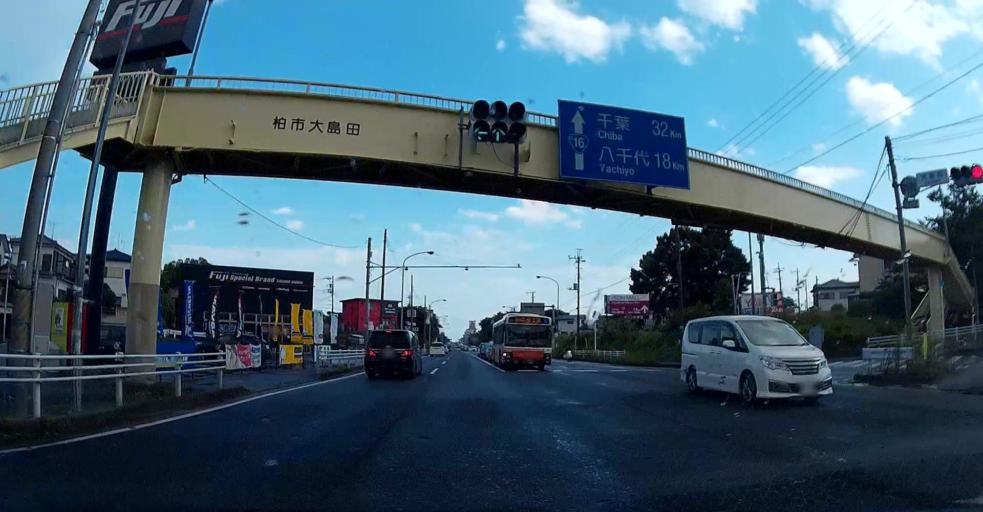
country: JP
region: Chiba
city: Abiko
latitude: 35.8373
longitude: 140.0063
